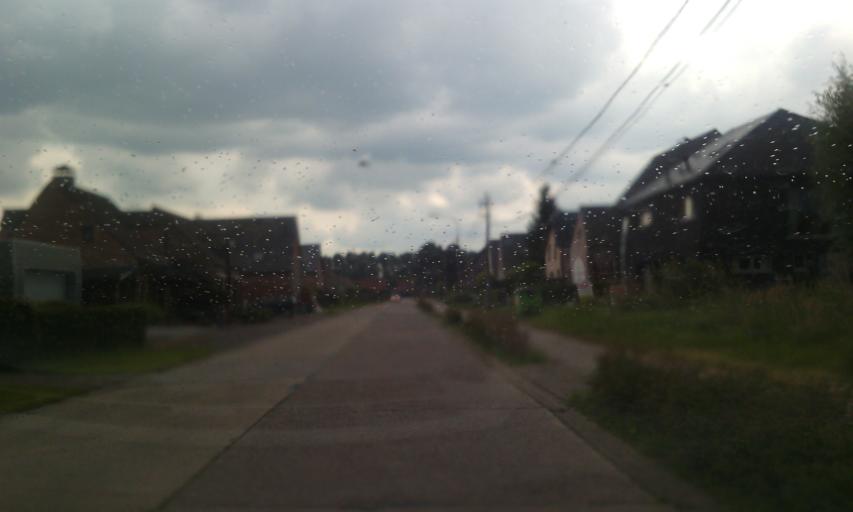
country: BE
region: Flanders
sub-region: Provincie Oost-Vlaanderen
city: Lokeren
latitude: 51.0877
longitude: 3.9174
